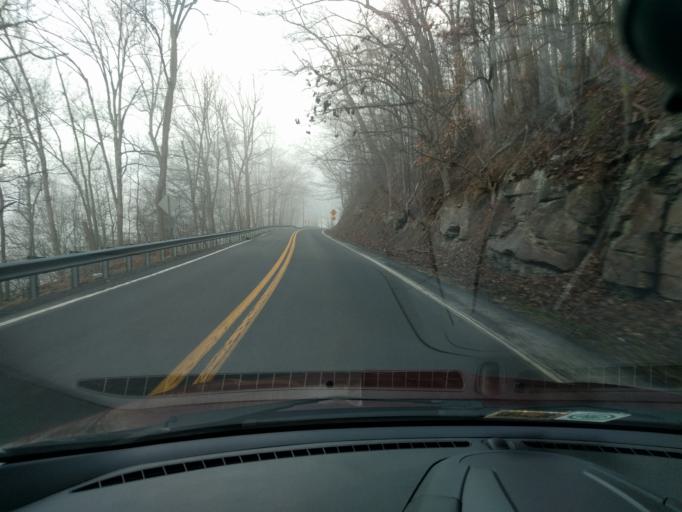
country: US
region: West Virginia
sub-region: Fayette County
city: Ansted
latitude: 38.1285
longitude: -81.1421
